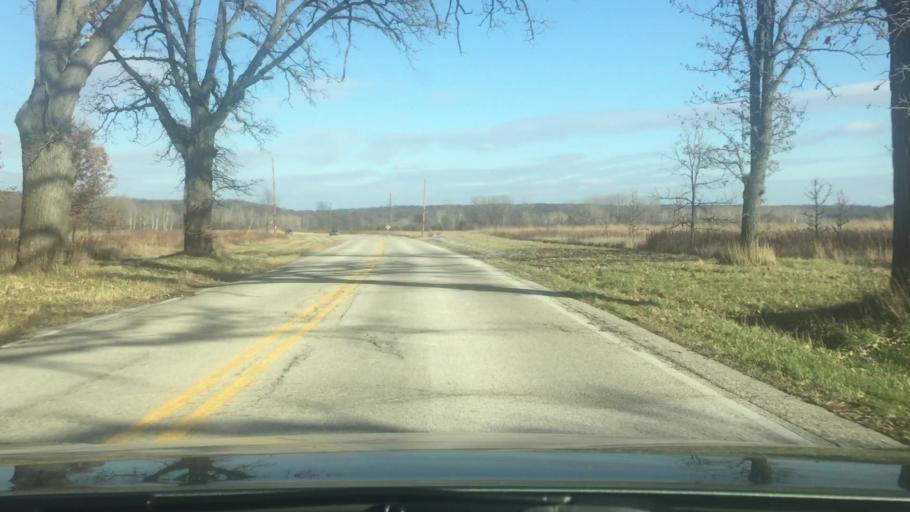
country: US
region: Wisconsin
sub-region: Waukesha County
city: Eagle
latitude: 42.9307
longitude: -88.4887
